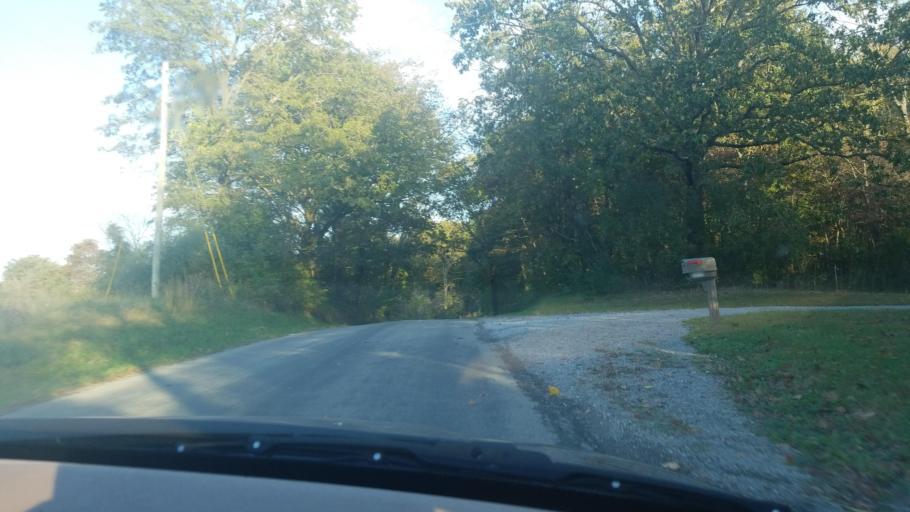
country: US
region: Illinois
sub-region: Williamson County
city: Marion
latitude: 37.7610
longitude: -88.7871
